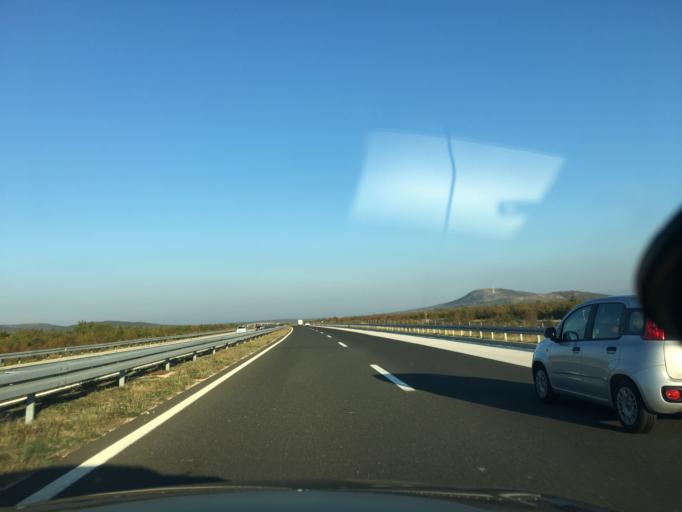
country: HR
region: Sibensko-Kniniska
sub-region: Grad Sibenik
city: Pirovac
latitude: 43.9201
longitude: 15.7390
